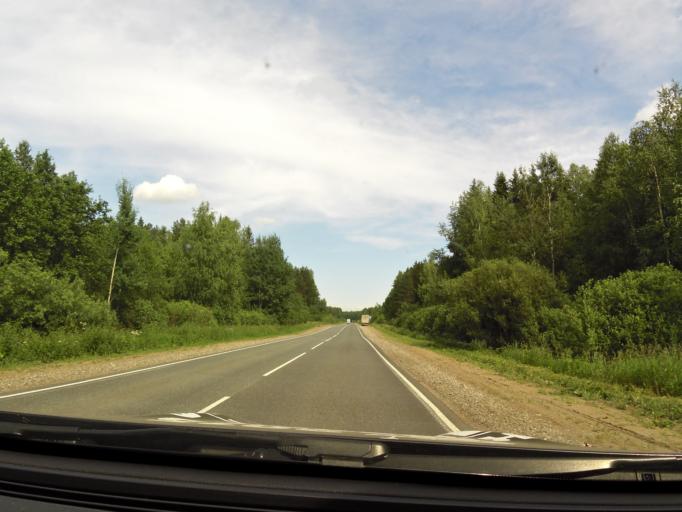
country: RU
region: Kirov
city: Slobodskoy
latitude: 58.7273
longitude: 50.2364
